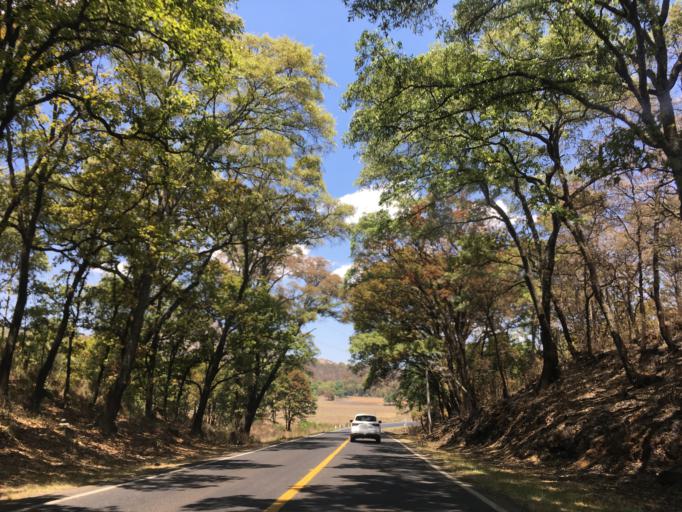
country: MX
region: Michoacan
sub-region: Chilchota
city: Tacuro (Santa Maria Tacuro)
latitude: 19.8118
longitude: -102.0280
